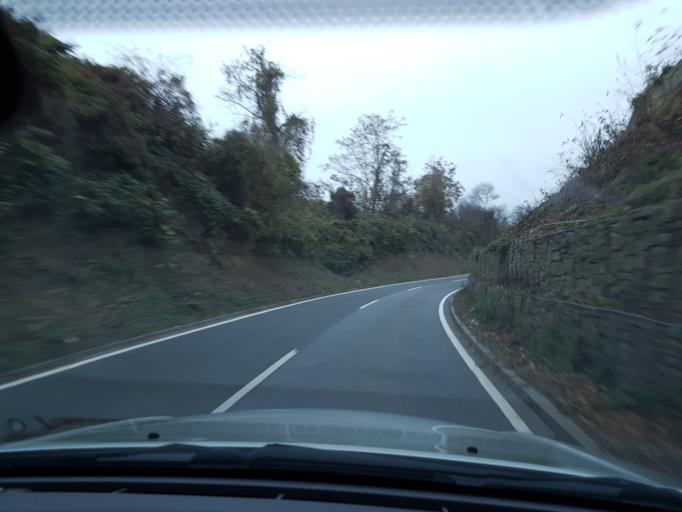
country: DE
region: Hesse
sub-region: Regierungsbezirk Darmstadt
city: Kiedrich
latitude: 50.0270
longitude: 8.0882
